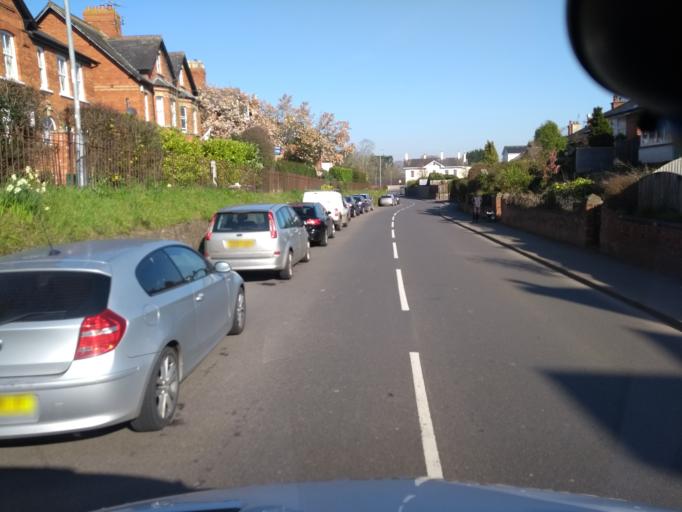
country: GB
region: England
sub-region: Somerset
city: Bishops Lydeard
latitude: 50.9822
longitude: -3.2384
